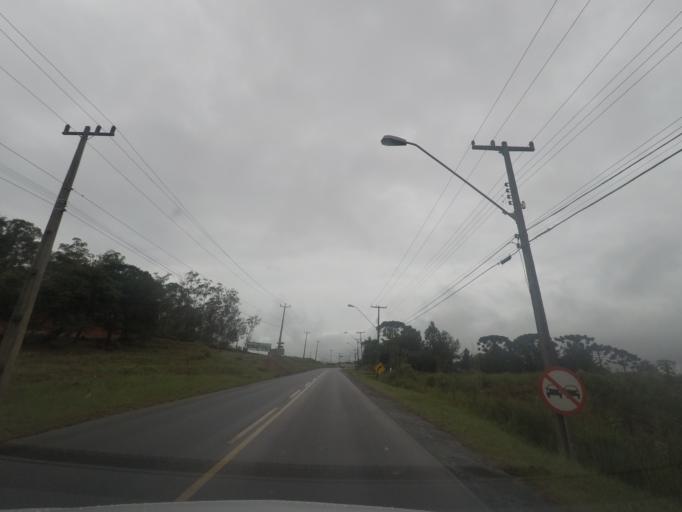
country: BR
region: Parana
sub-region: Campina Grande Do Sul
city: Campina Grande do Sul
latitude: -25.3262
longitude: -49.0783
